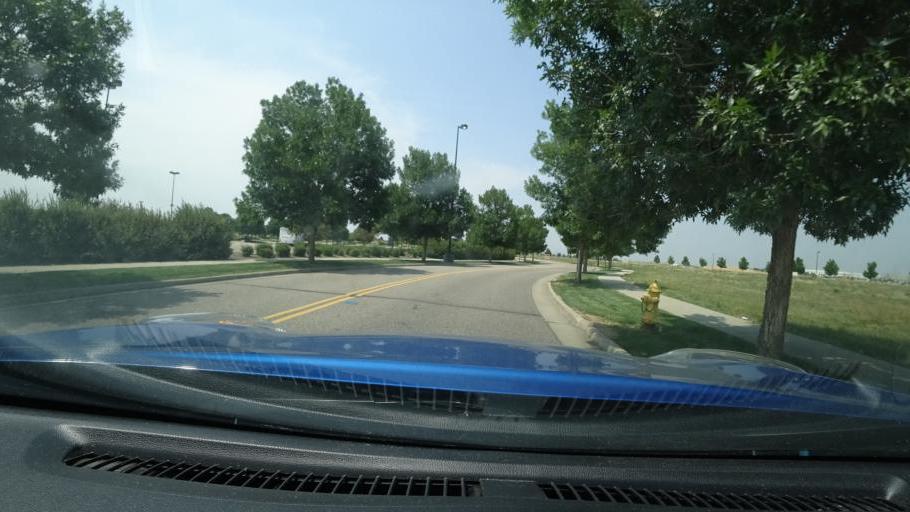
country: US
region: Colorado
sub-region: Adams County
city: Aurora
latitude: 39.7644
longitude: -104.7793
